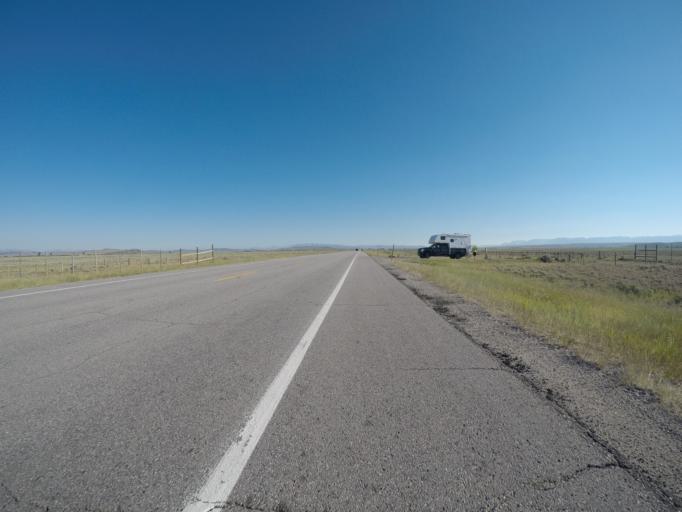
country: US
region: Wyoming
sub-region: Sublette County
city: Pinedale
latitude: 42.9559
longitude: -110.0870
